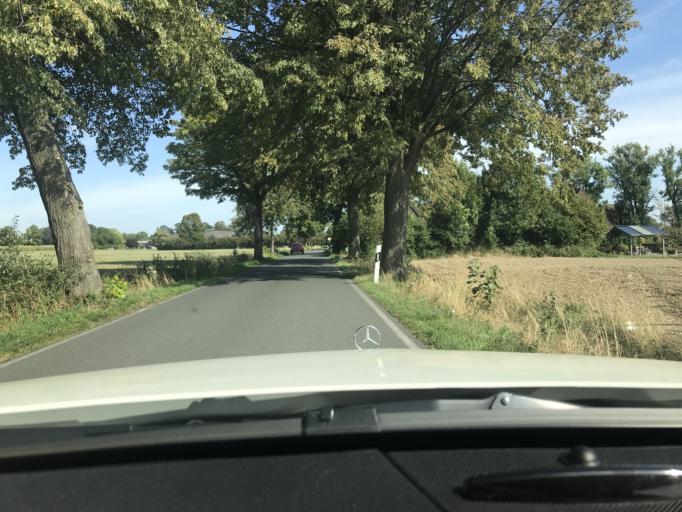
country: DE
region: North Rhine-Westphalia
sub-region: Regierungsbezirk Arnsberg
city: Bonen
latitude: 51.6065
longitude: 7.8244
